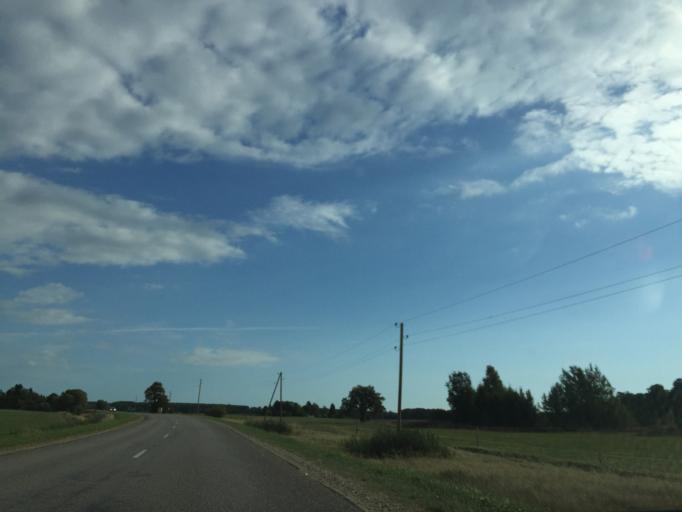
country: LV
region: Limbazu Rajons
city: Limbazi
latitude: 57.5047
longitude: 24.4980
